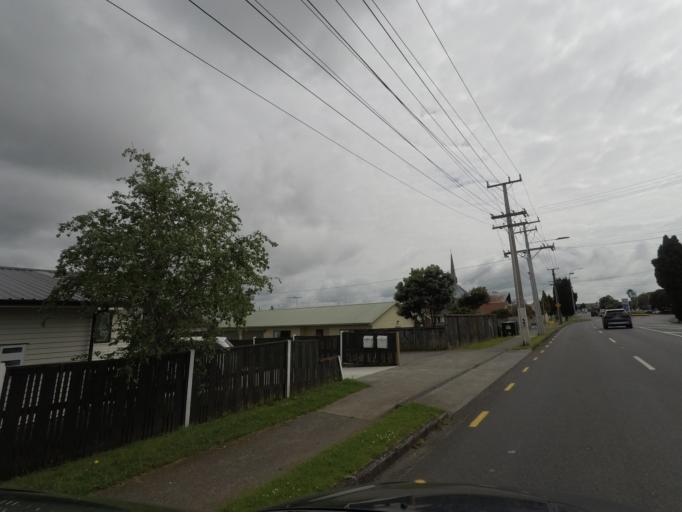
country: NZ
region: Auckland
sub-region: Auckland
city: Waitakere
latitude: -36.9104
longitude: 174.6619
